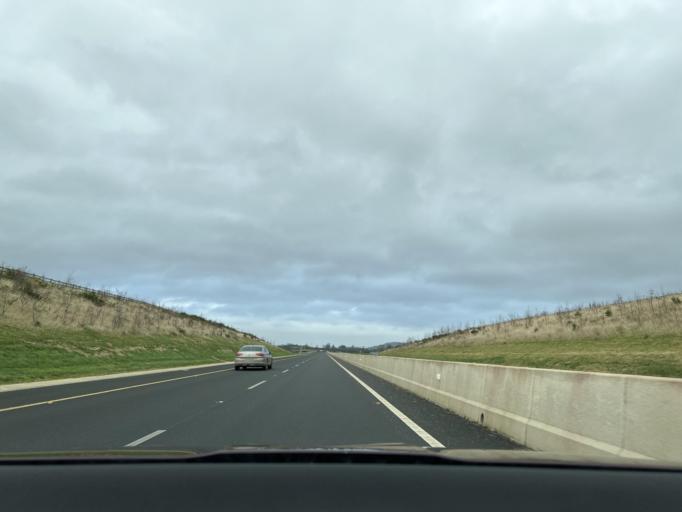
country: IE
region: Leinster
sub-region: Loch Garman
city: Ferns
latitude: 52.5562
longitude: -6.4757
